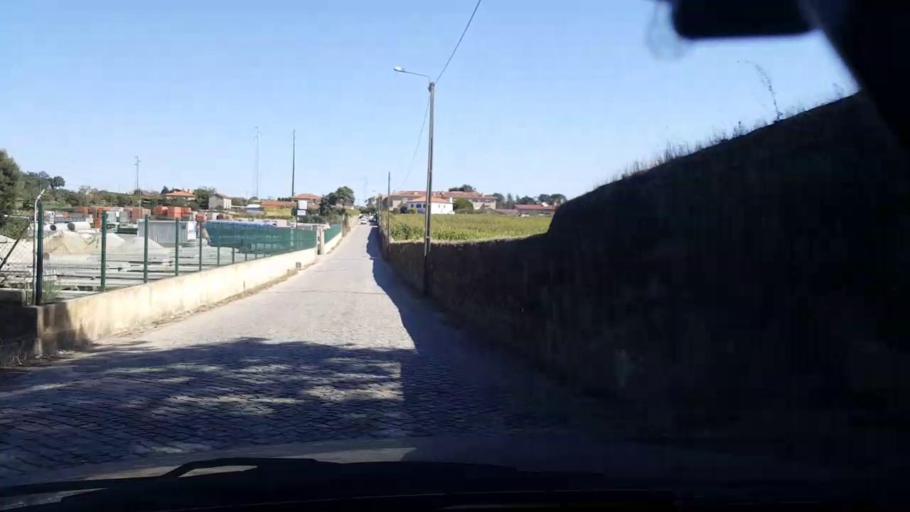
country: PT
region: Porto
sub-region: Vila do Conde
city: Arvore
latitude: 41.3113
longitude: -8.6823
